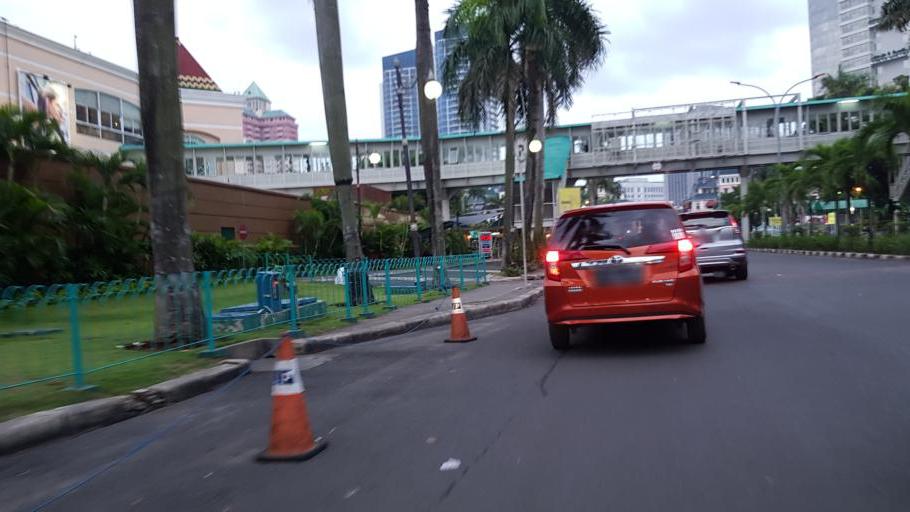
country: ID
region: West Java
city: Ciputat
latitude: -6.1896
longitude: 106.7343
